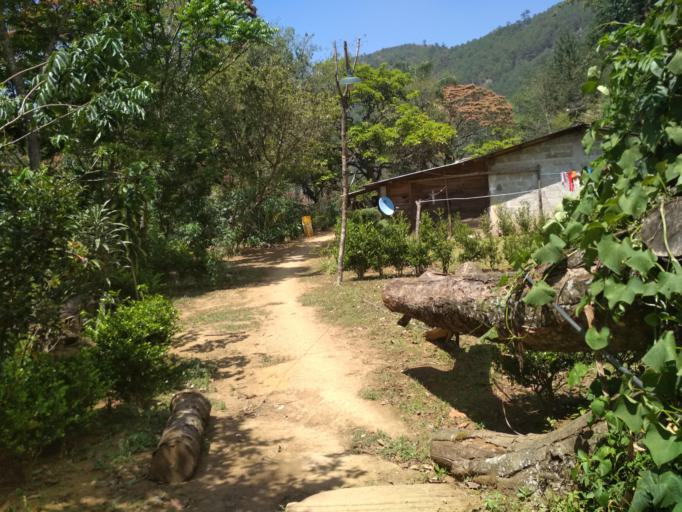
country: MX
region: Veracruz
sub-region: Tlilapan
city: Tonalixco
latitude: 18.7811
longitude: -97.0762
